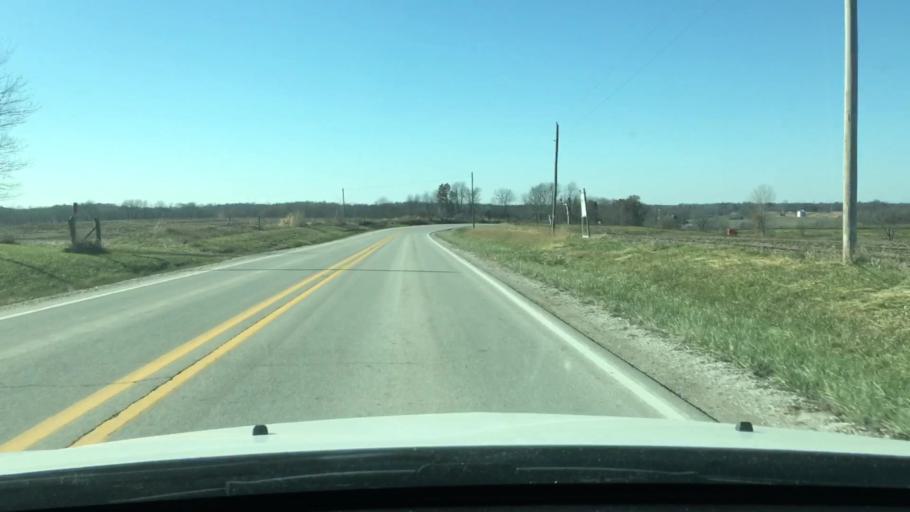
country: US
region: Illinois
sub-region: Pike County
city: Pittsfield
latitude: 39.6160
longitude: -90.7304
